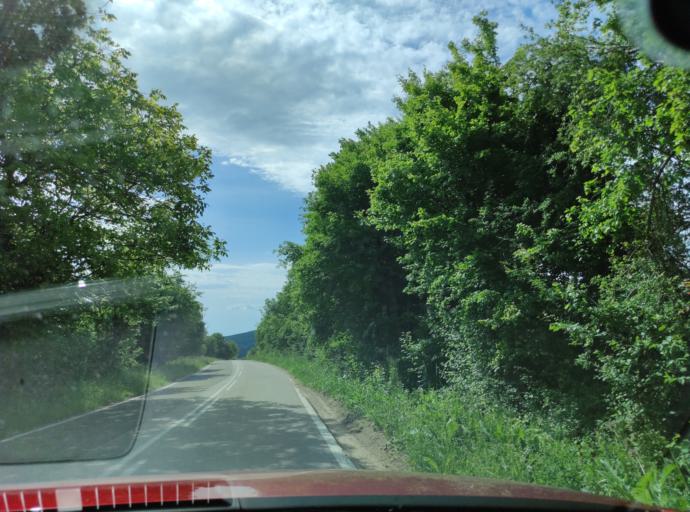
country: BG
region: Montana
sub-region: Obshtina Chiprovtsi
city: Chiprovtsi
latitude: 43.4767
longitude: 22.8404
